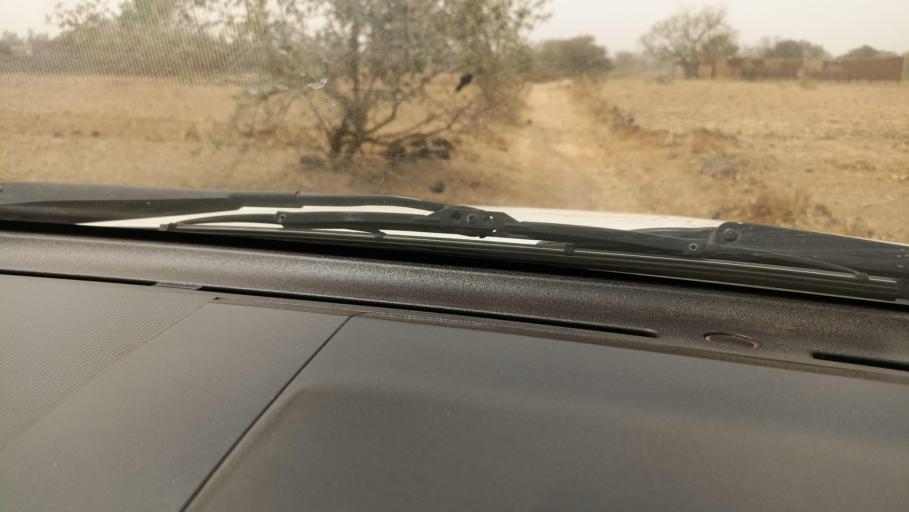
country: BF
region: Boucle du Mouhoun
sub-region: Province du Nayala
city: Toma
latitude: 12.8547
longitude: -2.7968
